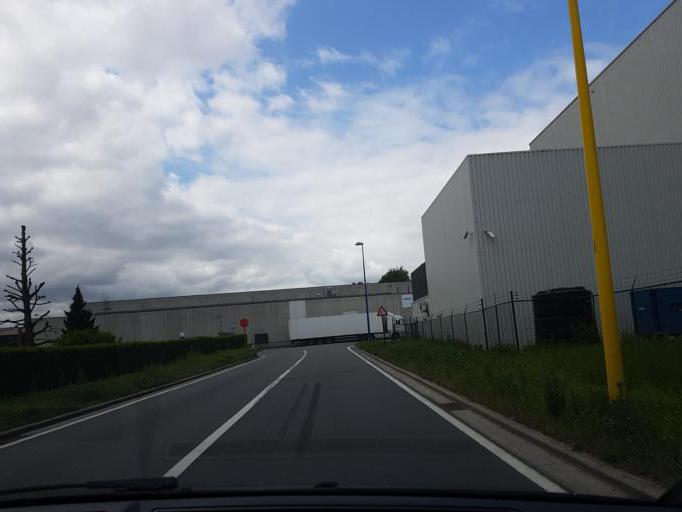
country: BE
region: Flanders
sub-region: Provincie Vlaams-Brabant
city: Vilvoorde
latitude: 50.9440
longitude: 4.4110
